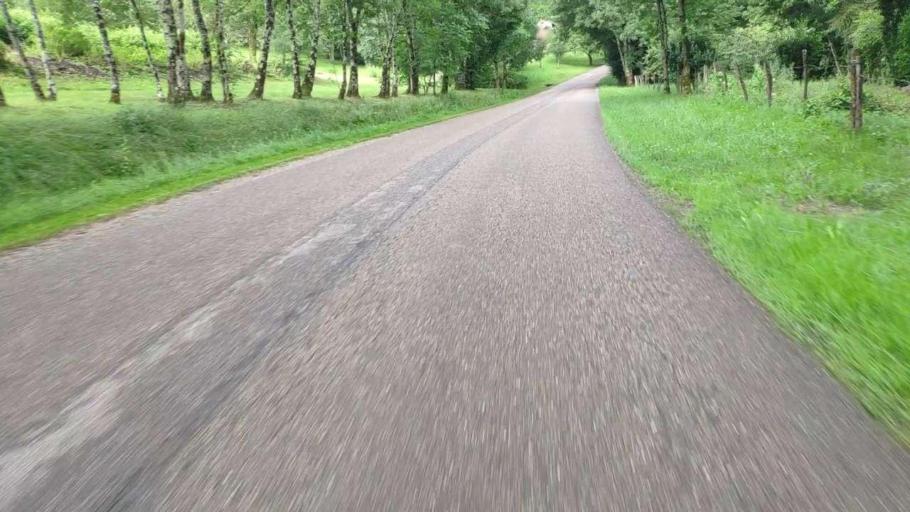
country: FR
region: Franche-Comte
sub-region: Departement du Jura
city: Poligny
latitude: 46.8010
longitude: 5.6169
